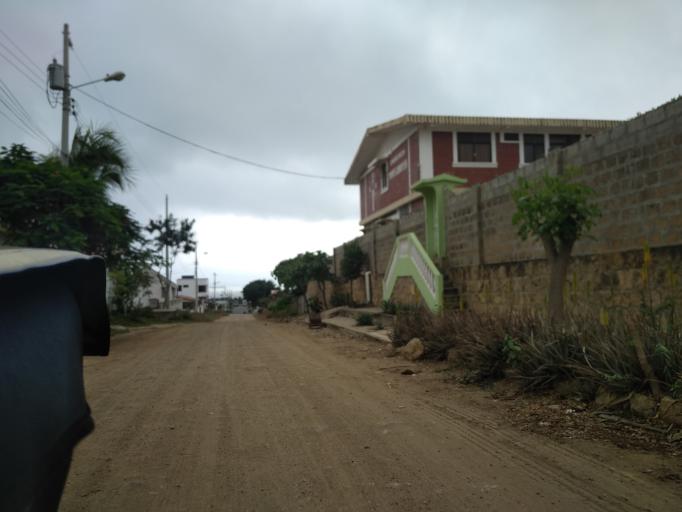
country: EC
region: Santa Elena
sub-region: Canton Santa Elena
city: Santa Elena
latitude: -2.2042
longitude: -80.8686
